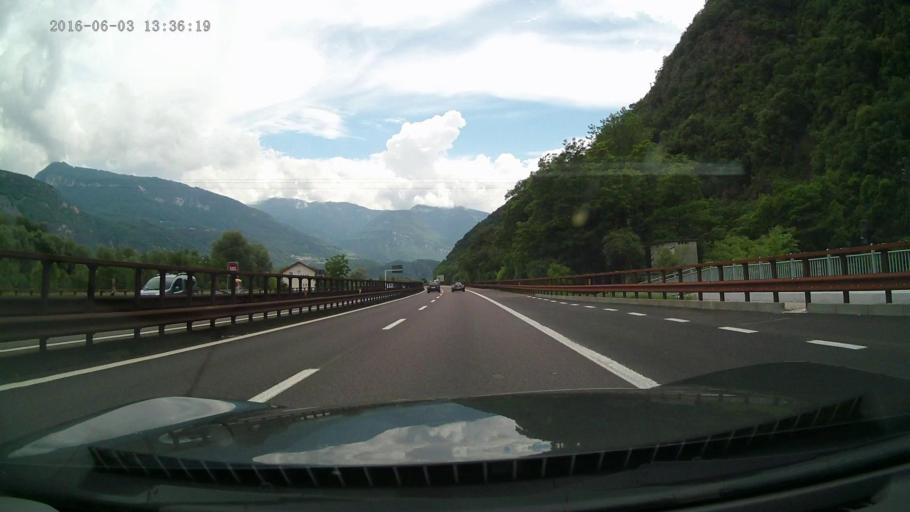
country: IT
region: Trentino-Alto Adige
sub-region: Bolzano
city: Ora
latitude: 46.3737
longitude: 11.2904
